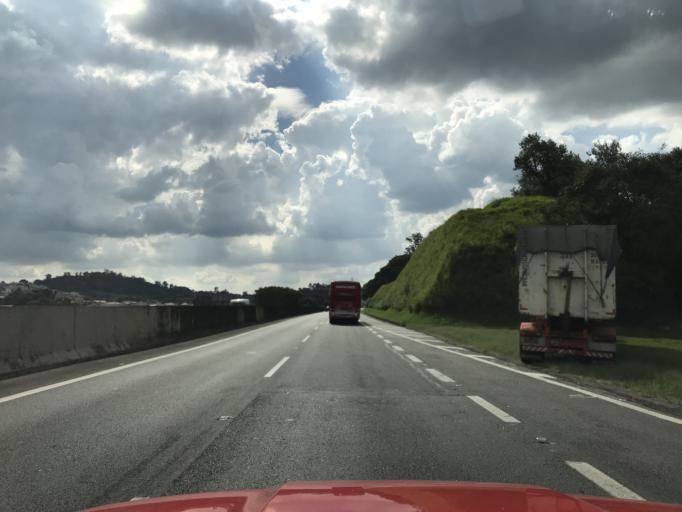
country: BR
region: Sao Paulo
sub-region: Vinhedo
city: Vinhedo
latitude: -23.0410
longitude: -47.0073
